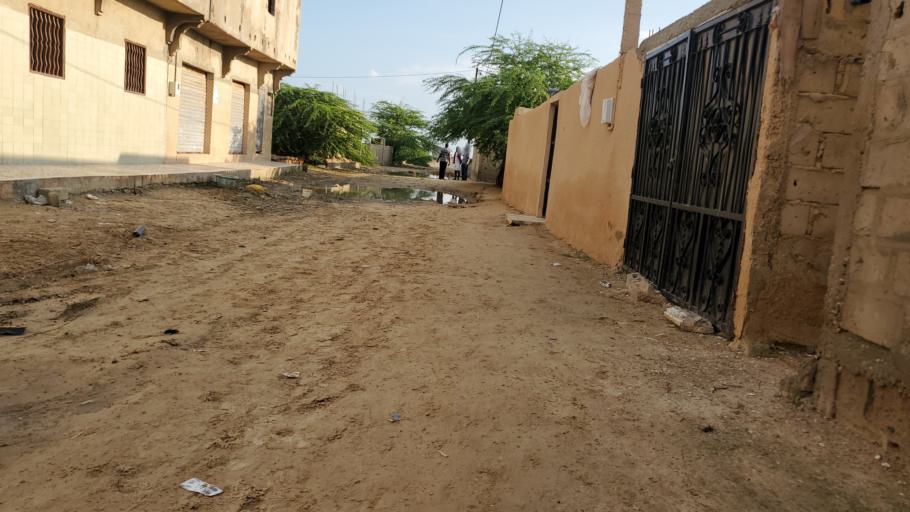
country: SN
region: Saint-Louis
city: Saint-Louis
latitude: 16.0594
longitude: -16.4188
